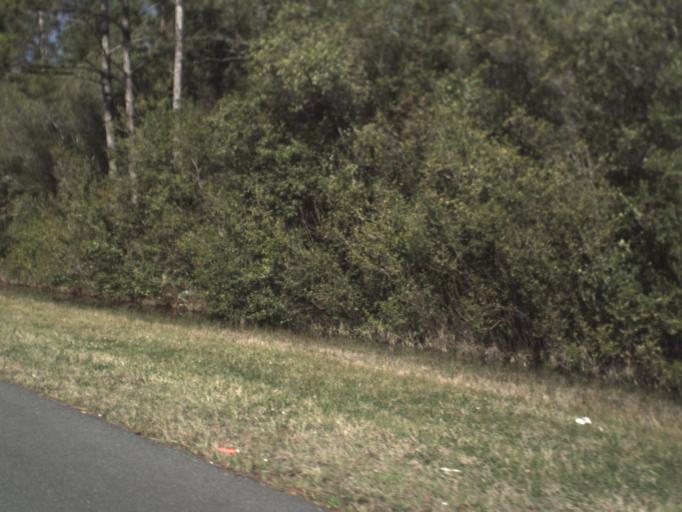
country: US
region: Florida
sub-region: Bay County
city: Callaway
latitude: 30.1528
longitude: -85.5269
